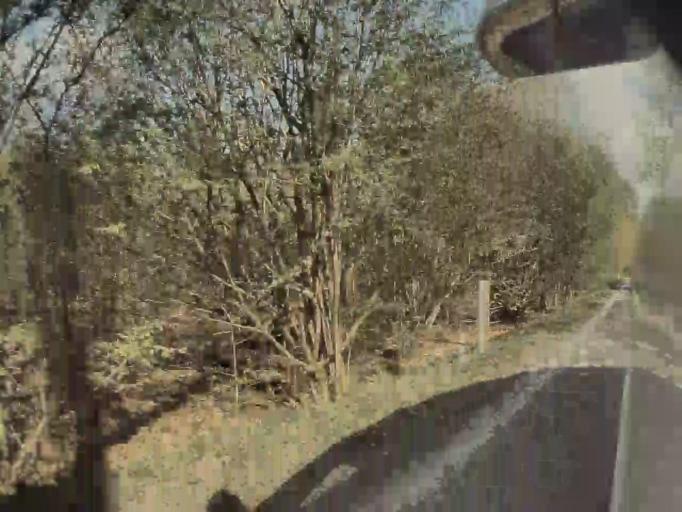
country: BE
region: Wallonia
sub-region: Province du Luxembourg
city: Tellin
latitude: 50.0239
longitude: 5.2027
